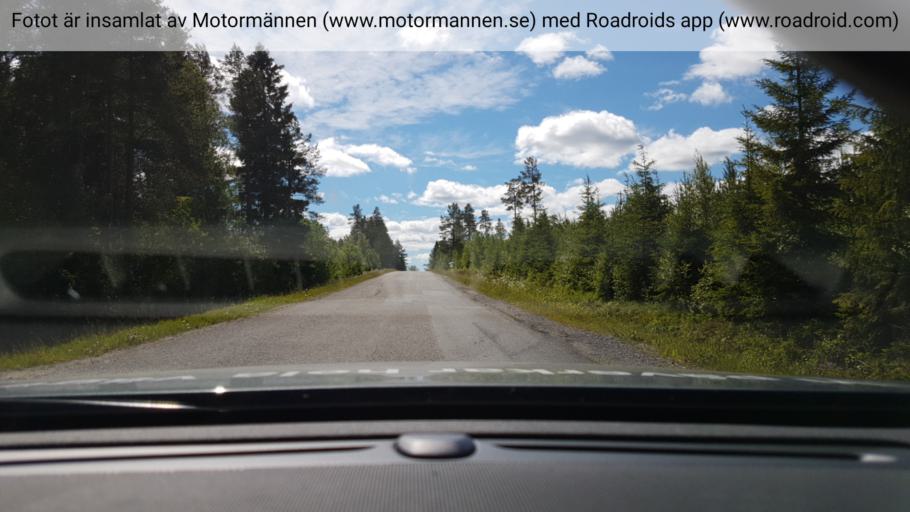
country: SE
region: Vaesterbotten
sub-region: Skelleftea Kommun
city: Burea
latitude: 64.4260
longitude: 21.3532
